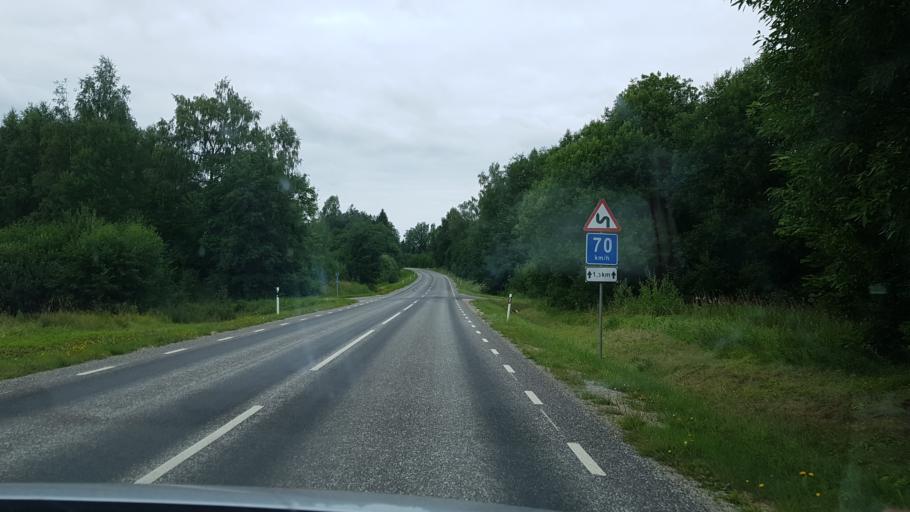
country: EE
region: Vorumaa
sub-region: Antsla vald
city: Vana-Antsla
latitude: 58.0122
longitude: 26.5965
